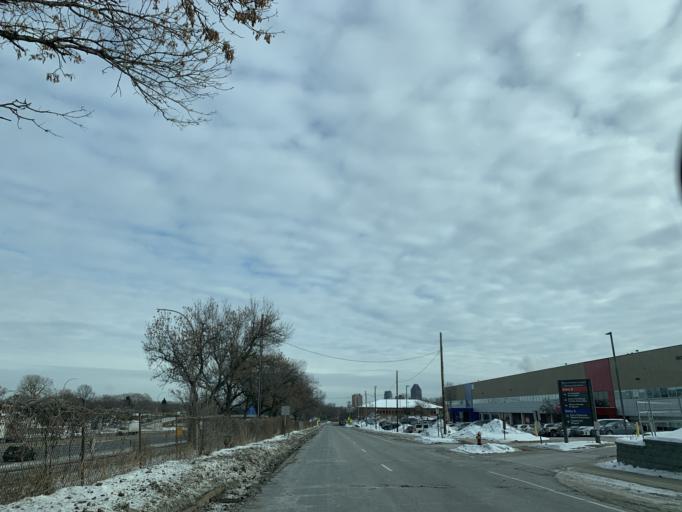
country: US
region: Minnesota
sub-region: Ramsey County
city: Saint Paul
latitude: 44.9513
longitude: -93.1241
